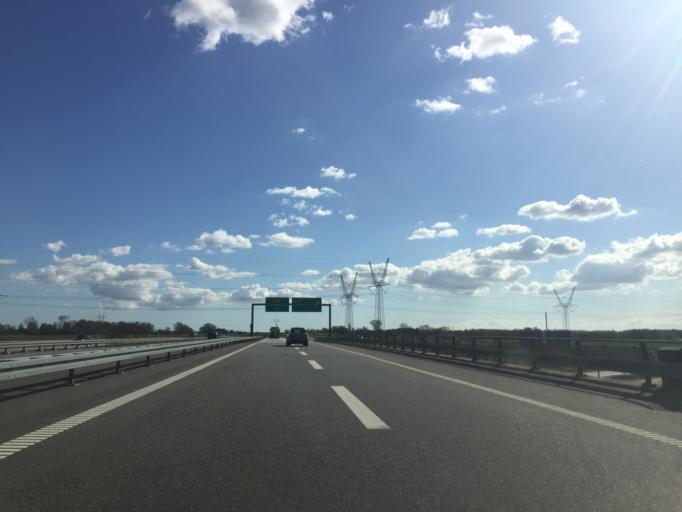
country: DK
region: South Denmark
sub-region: Odense Kommune
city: Neder Holluf
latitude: 55.3499
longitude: 10.4569
